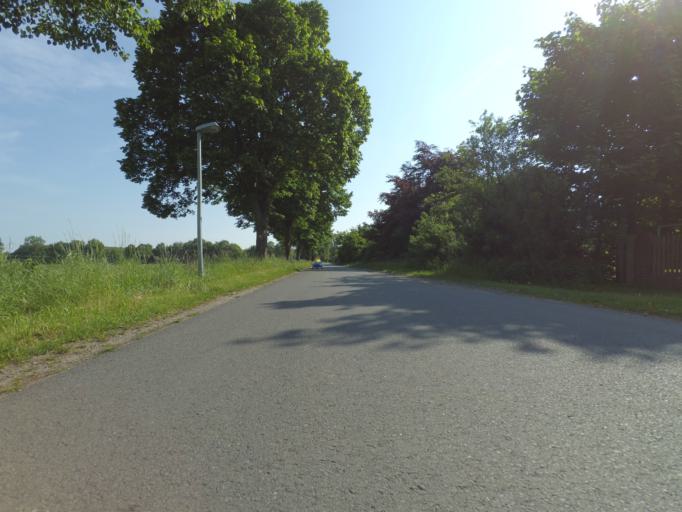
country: DE
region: Lower Saxony
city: Burgdorf
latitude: 52.4189
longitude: 10.0045
